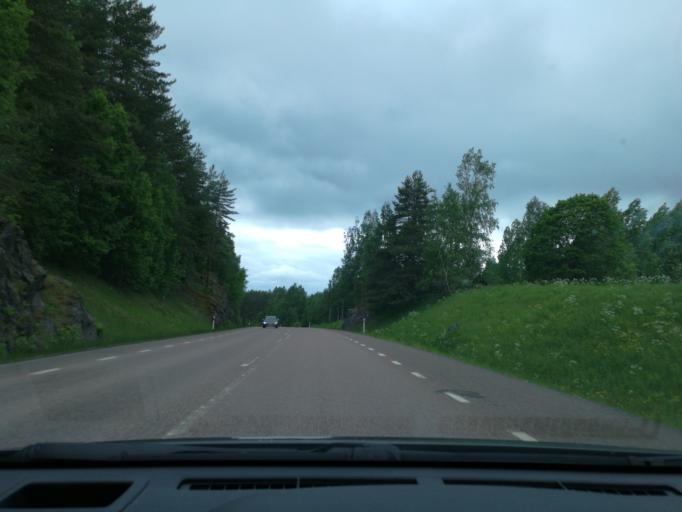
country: SE
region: Dalarna
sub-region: Smedjebackens Kommun
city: Smedjebacken
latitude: 60.1314
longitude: 15.4371
